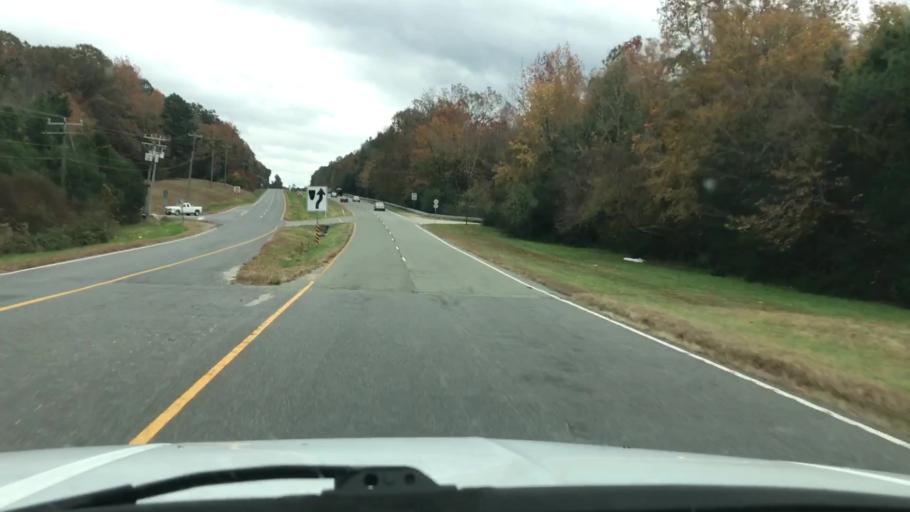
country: US
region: Virginia
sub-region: Henrico County
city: Short Pump
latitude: 37.6073
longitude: -77.7279
